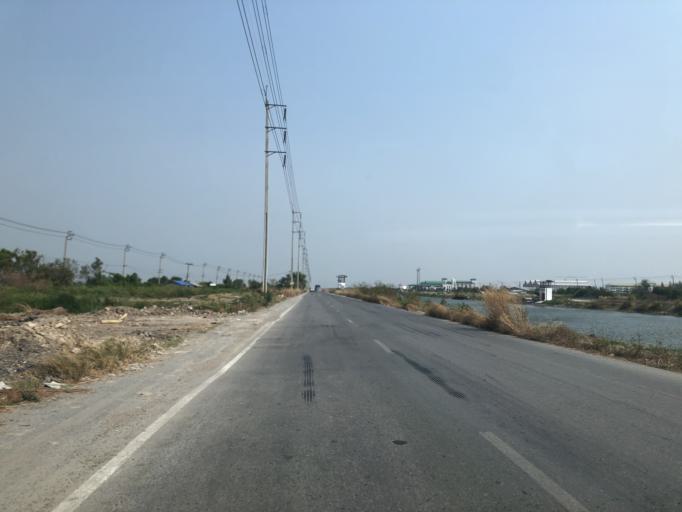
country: TH
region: Samut Prakan
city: Bang Bo District
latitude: 13.5164
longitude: 100.7461
